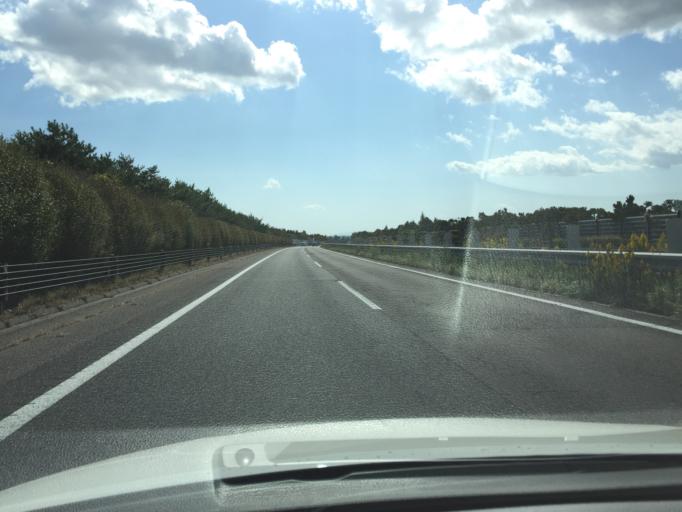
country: JP
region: Fukushima
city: Koriyama
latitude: 37.3860
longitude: 140.3124
